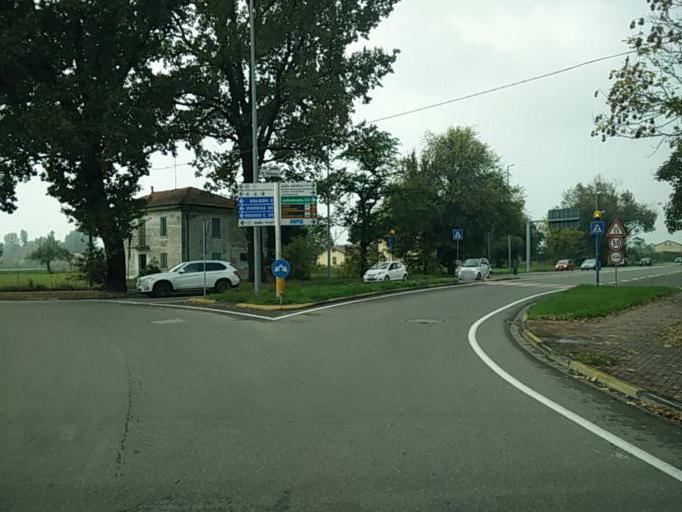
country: IT
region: Emilia-Romagna
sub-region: Provincia di Modena
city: Carpi Centro
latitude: 44.7812
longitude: 10.8668
